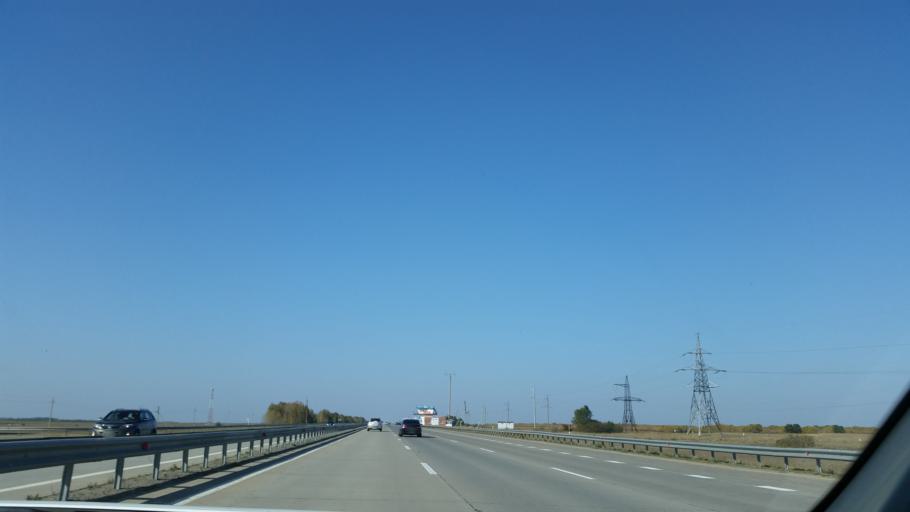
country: KZ
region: Astana Qalasy
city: Astana
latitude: 51.3016
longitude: 71.3553
